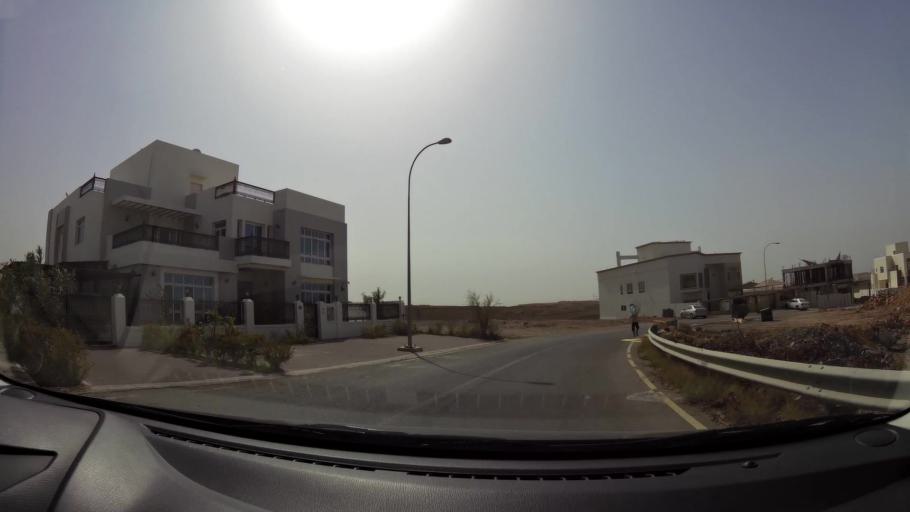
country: OM
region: Muhafazat Masqat
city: Bawshar
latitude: 23.5558
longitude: 58.3432
